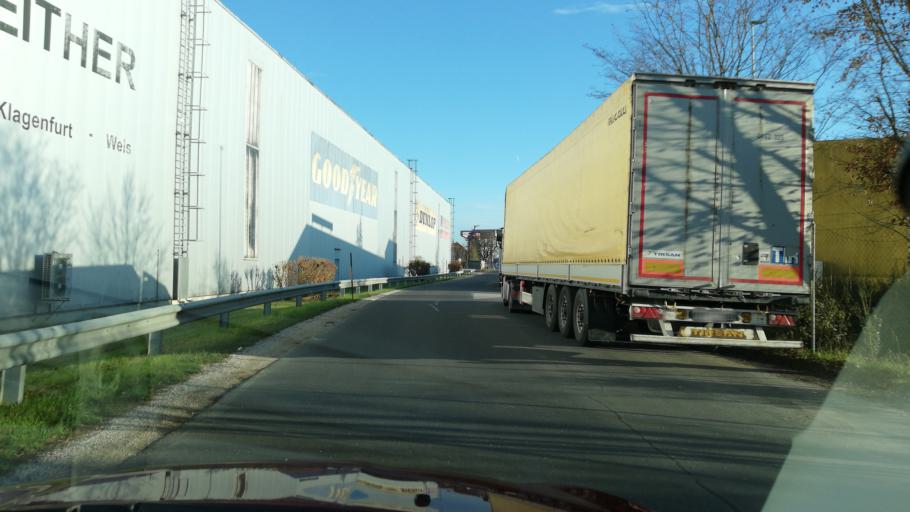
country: AT
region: Upper Austria
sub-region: Wels Stadt
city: Wels
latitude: 48.1871
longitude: 14.0604
